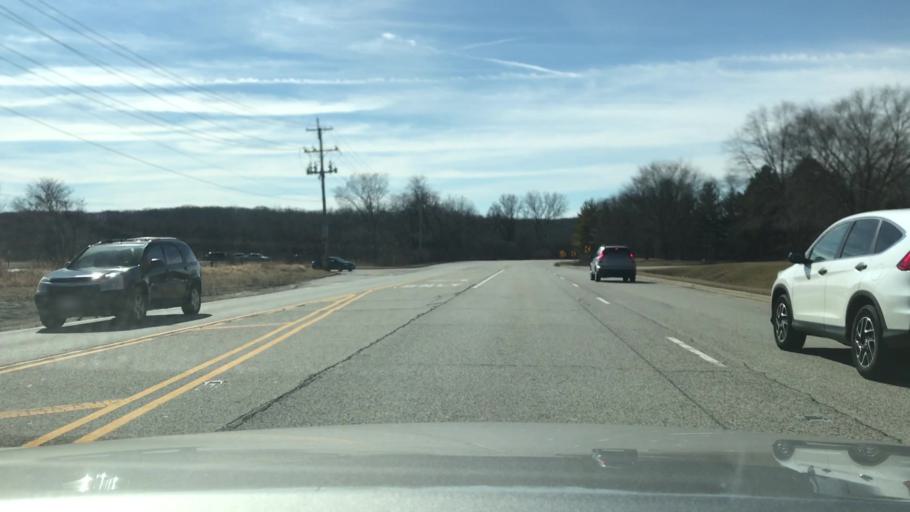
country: US
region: Illinois
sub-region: DuPage County
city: Lisle
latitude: 41.8285
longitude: -88.0545
